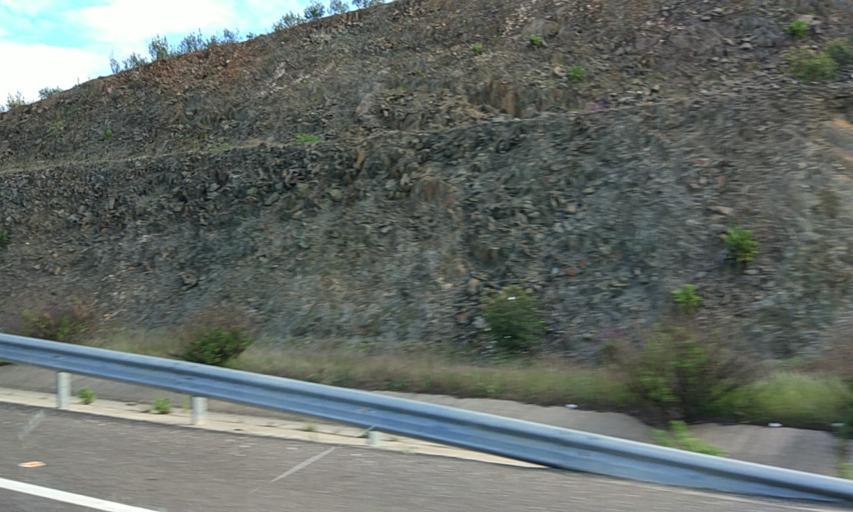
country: ES
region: Extremadura
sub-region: Provincia de Caceres
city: Casas de Don Gomez
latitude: 40.0260
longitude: -6.6061
